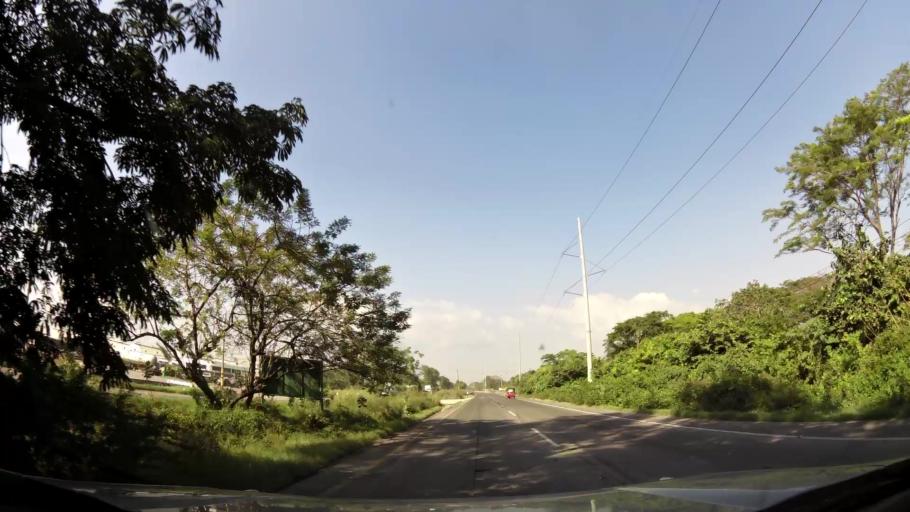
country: GT
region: Escuintla
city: Puerto San Jose
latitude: 13.9600
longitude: -90.7884
